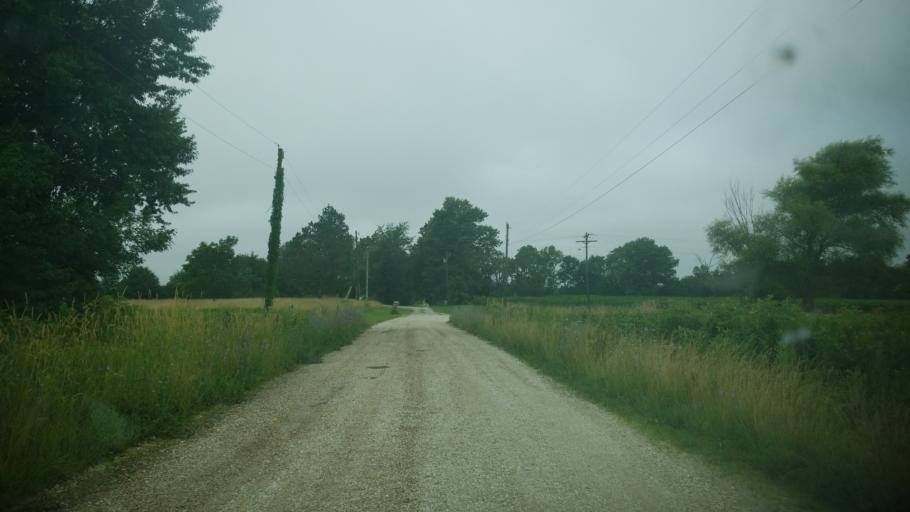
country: US
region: Missouri
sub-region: Pike County
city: Bowling Green
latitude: 39.3494
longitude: -91.2608
